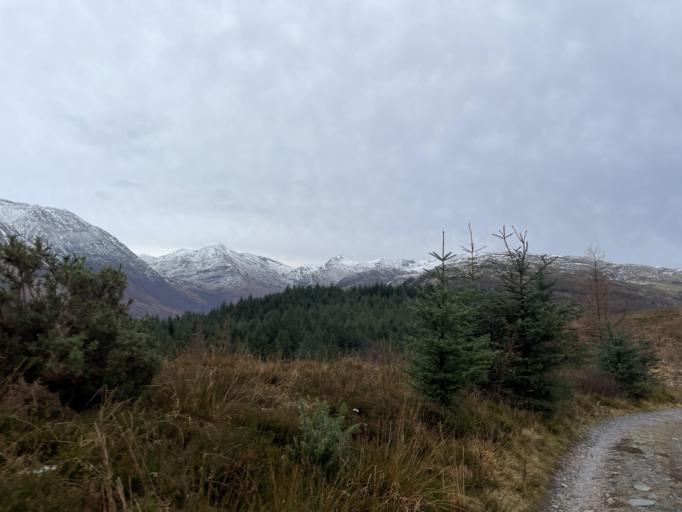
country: GB
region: Scotland
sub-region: Highland
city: Fort William
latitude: 56.8142
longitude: -5.0934
